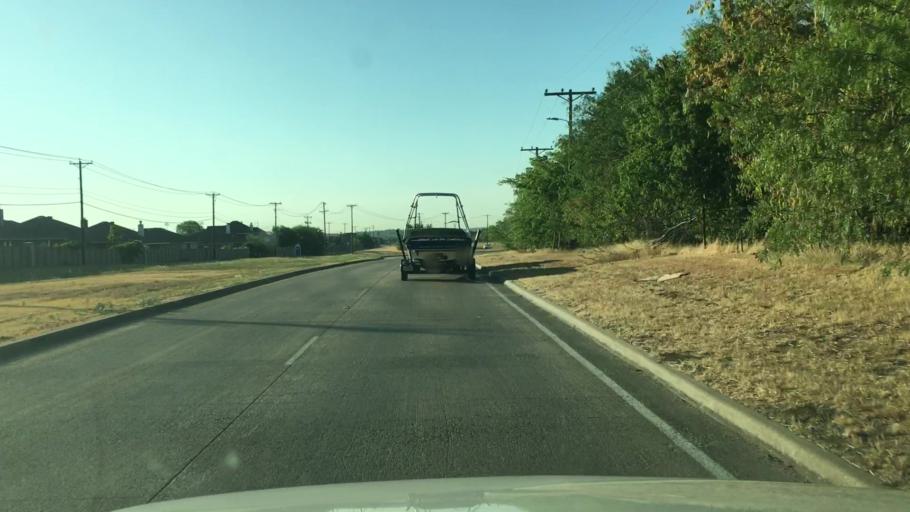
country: US
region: Texas
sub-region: Johnson County
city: Burleson
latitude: 32.5341
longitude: -97.3553
